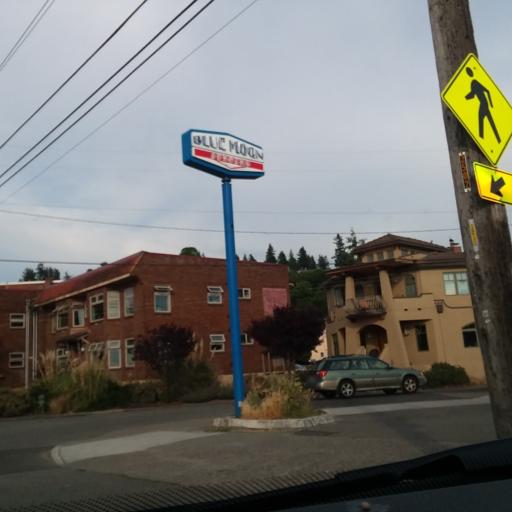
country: US
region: Washington
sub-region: King County
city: Seattle
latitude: 47.5811
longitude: -122.4055
